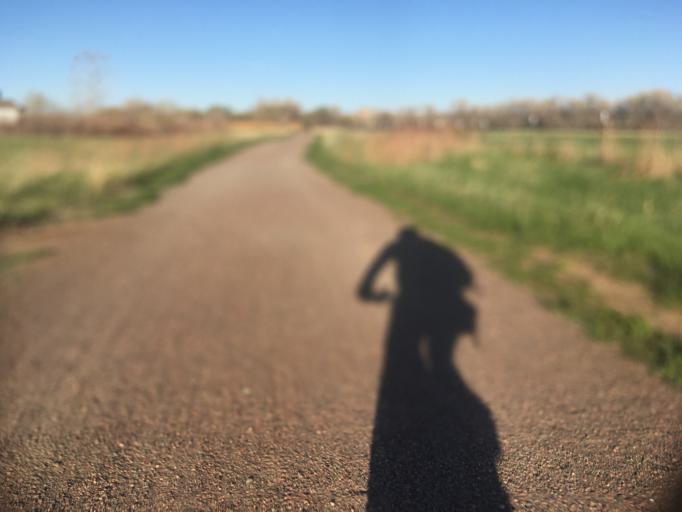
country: US
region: Colorado
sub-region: Boulder County
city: Lafayette
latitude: 39.9797
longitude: -105.0824
